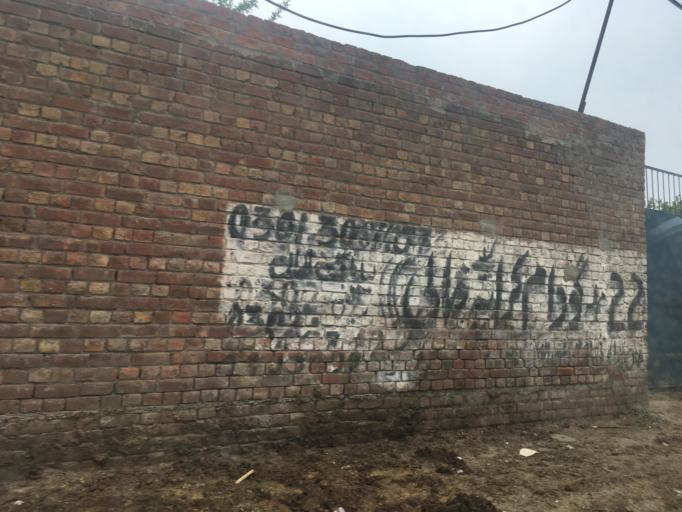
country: PK
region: Punjab
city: Lahore
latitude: 31.6171
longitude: 74.3675
